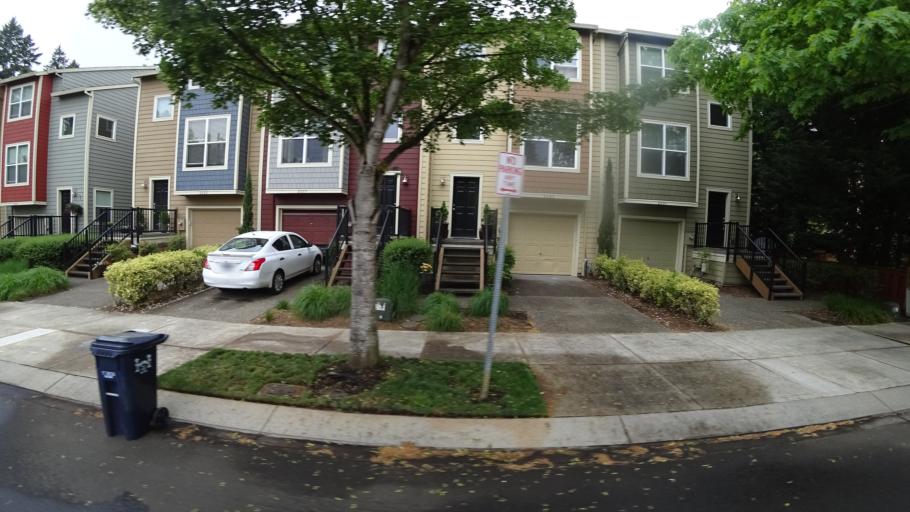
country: US
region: Oregon
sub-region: Washington County
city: Rockcreek
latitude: 45.5344
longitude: -122.8901
